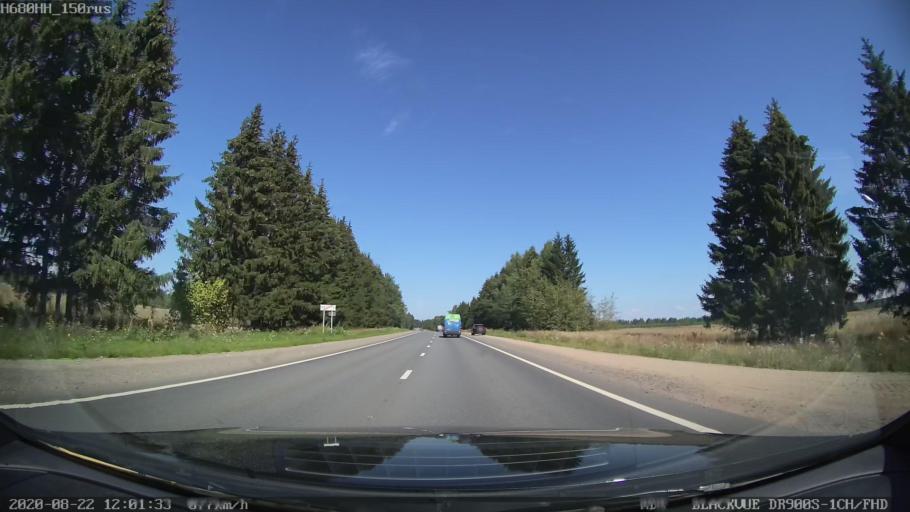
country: RU
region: Tverskaya
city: Rameshki
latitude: 57.2305
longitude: 36.0999
